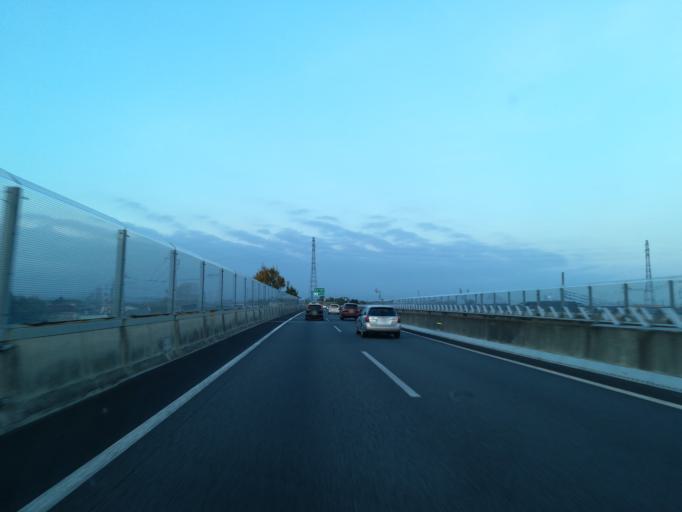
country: JP
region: Gunma
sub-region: Sawa-gun
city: Tamamura
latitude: 36.3437
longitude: 139.1389
